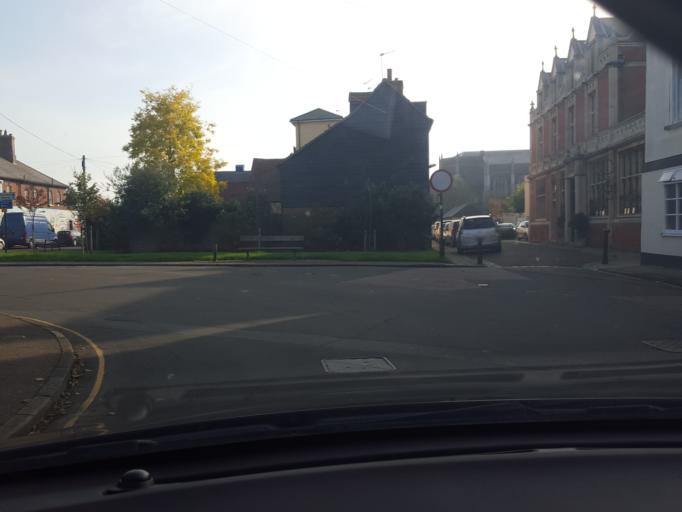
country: GB
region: England
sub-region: Essex
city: Harwich
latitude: 51.9471
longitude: 1.2883
